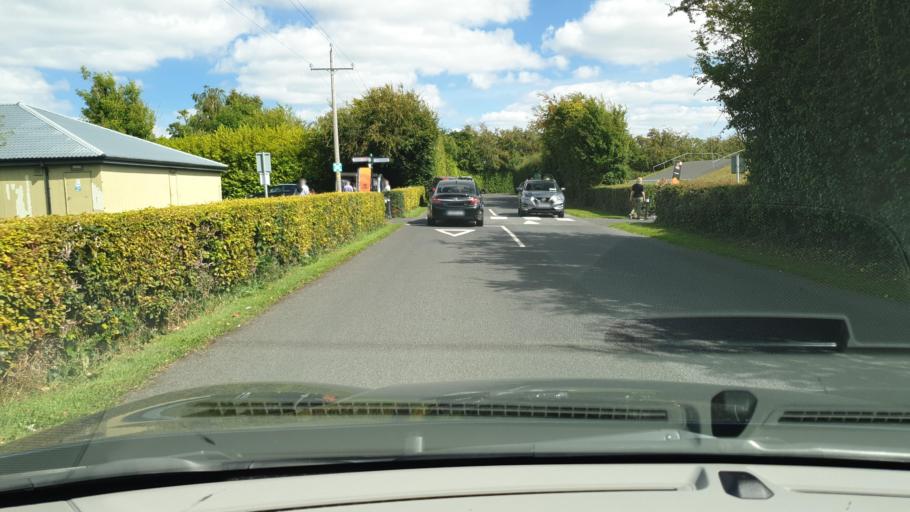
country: IE
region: Leinster
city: Lucan
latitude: 53.3669
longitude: -6.4649
